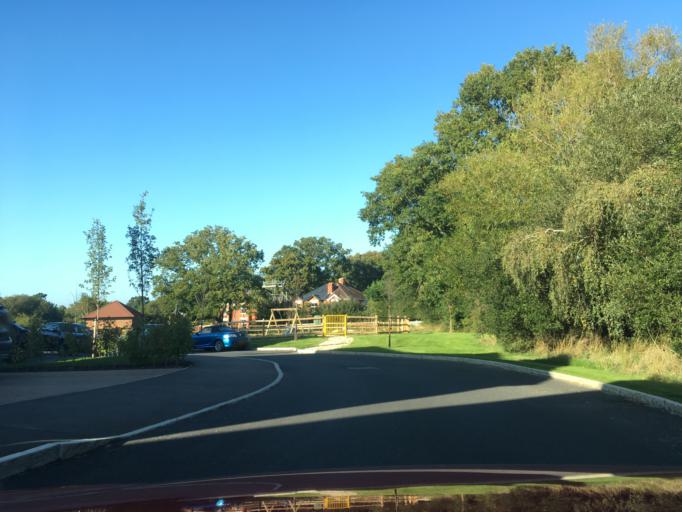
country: GB
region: England
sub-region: Hampshire
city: Swanmore
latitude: 50.9341
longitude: -1.1963
